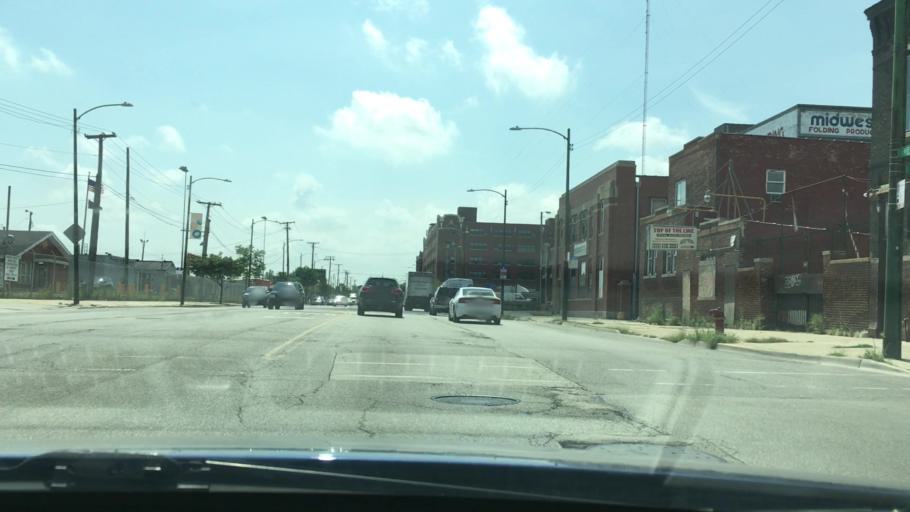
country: US
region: Illinois
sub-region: Cook County
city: Chicago
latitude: 41.8630
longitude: -87.6860
